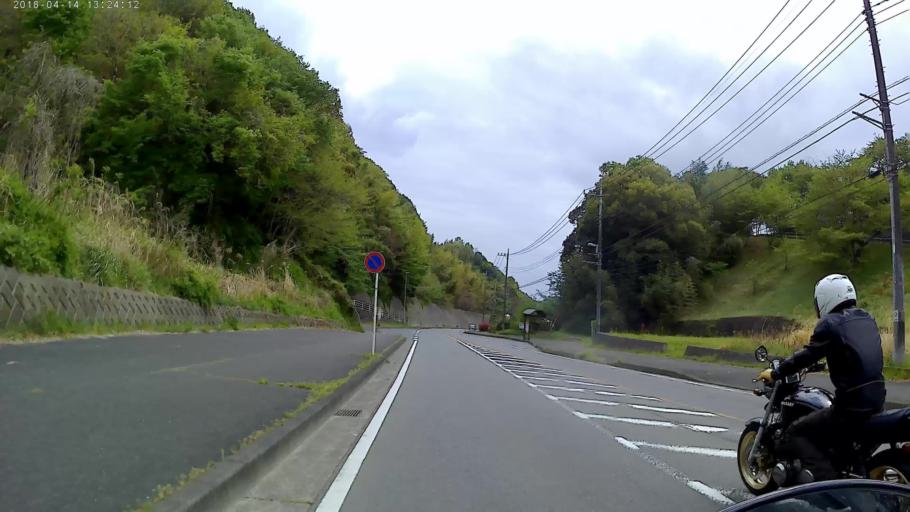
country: JP
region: Kanagawa
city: Hadano
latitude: 35.3350
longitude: 139.2196
